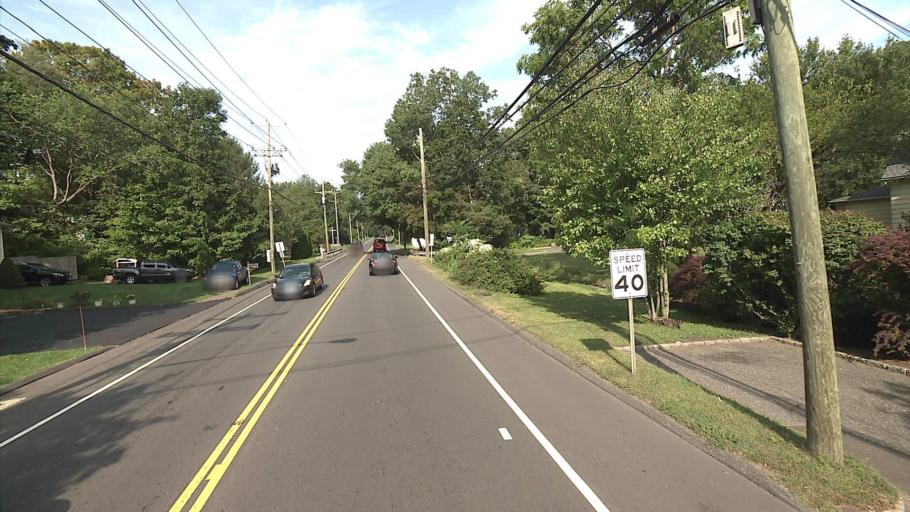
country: US
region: Connecticut
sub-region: Fairfield County
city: Norwalk
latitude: 41.1286
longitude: -73.4375
